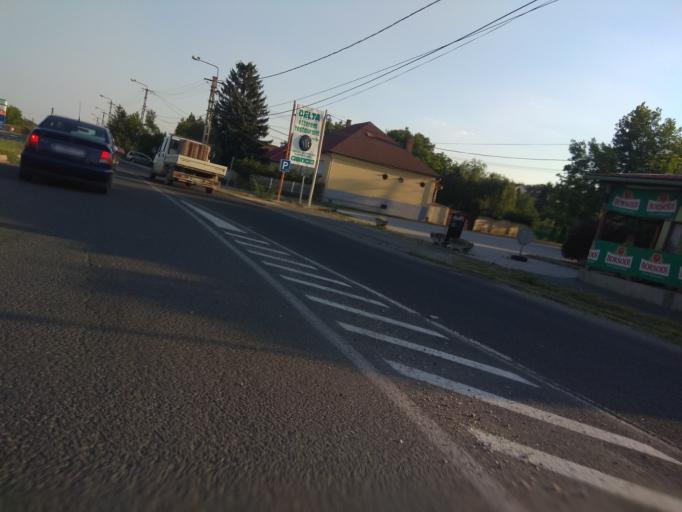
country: HU
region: Borsod-Abauj-Zemplen
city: Nyekladhaza
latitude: 47.9874
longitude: 20.8311
